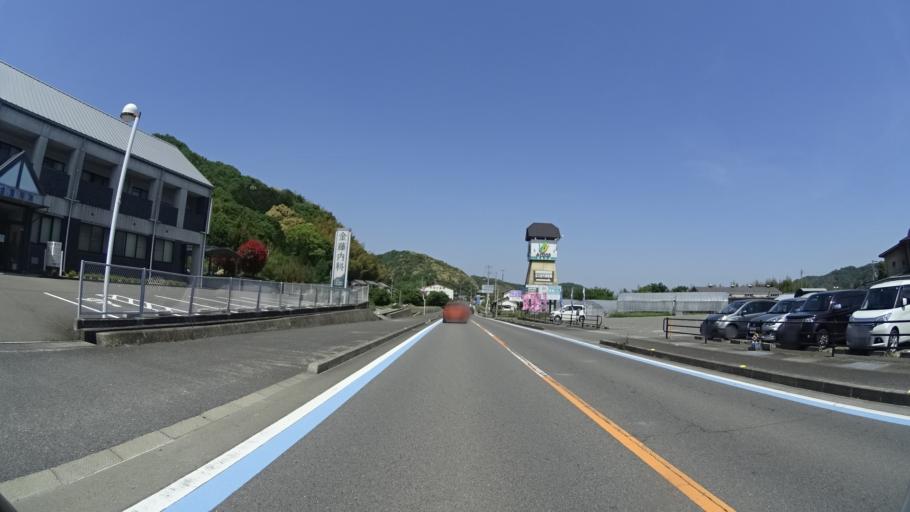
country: JP
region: Ehime
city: Hojo
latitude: 34.0224
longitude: 132.9435
